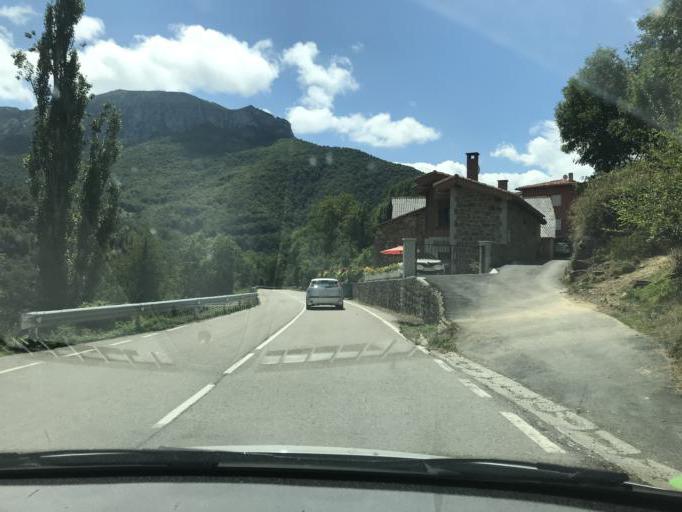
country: ES
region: Cantabria
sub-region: Provincia de Cantabria
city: Cabezon de Liebana
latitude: 43.0761
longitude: -4.4918
